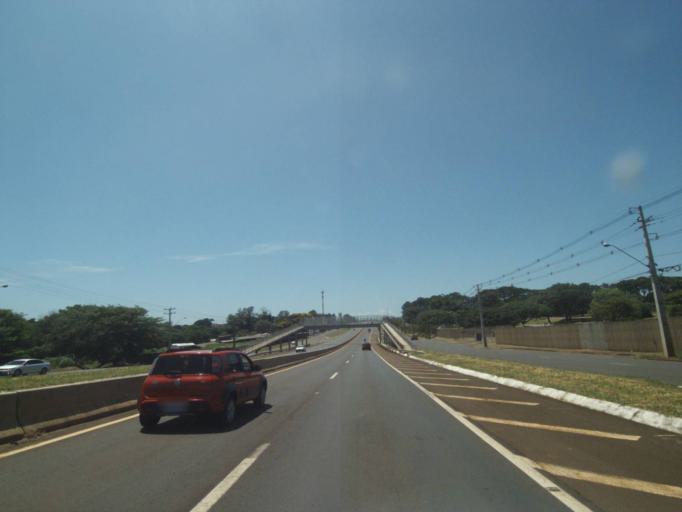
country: BR
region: Parana
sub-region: Londrina
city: Londrina
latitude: -23.3534
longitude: -51.1624
